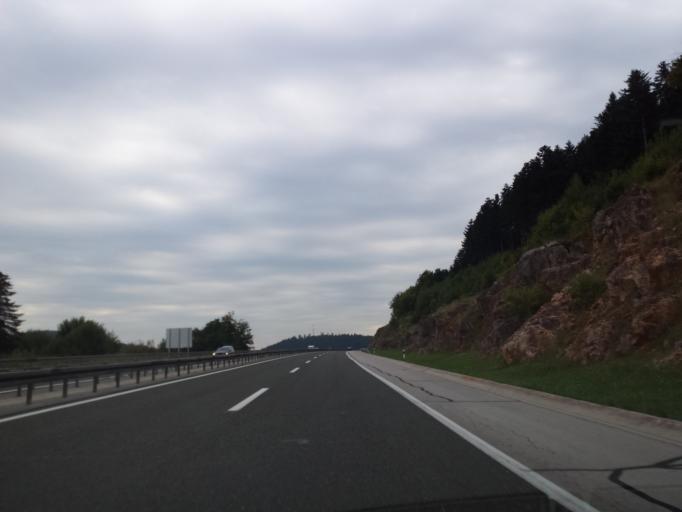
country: HR
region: Licko-Senjska
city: Otocac
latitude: 44.8576
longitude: 15.2184
